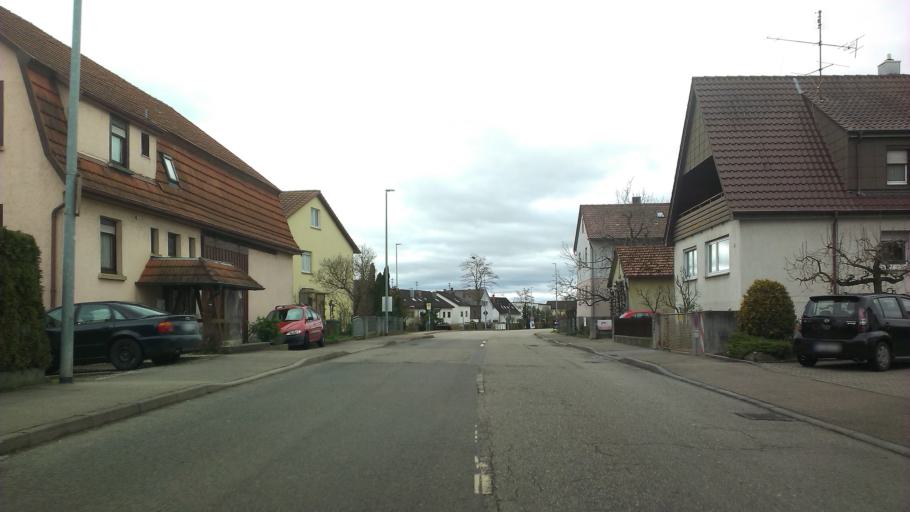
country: DE
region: Baden-Wuerttemberg
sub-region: Regierungsbezirk Stuttgart
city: Sersheim
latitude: 48.9599
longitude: 9.0093
